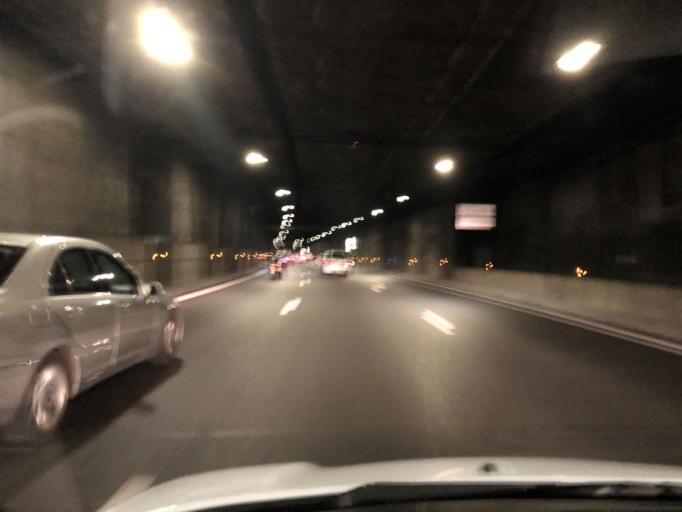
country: FR
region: Provence-Alpes-Cote d'Azur
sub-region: Departement des Bouches-du-Rhone
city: Marseille 13
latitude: 43.3168
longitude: 5.4223
